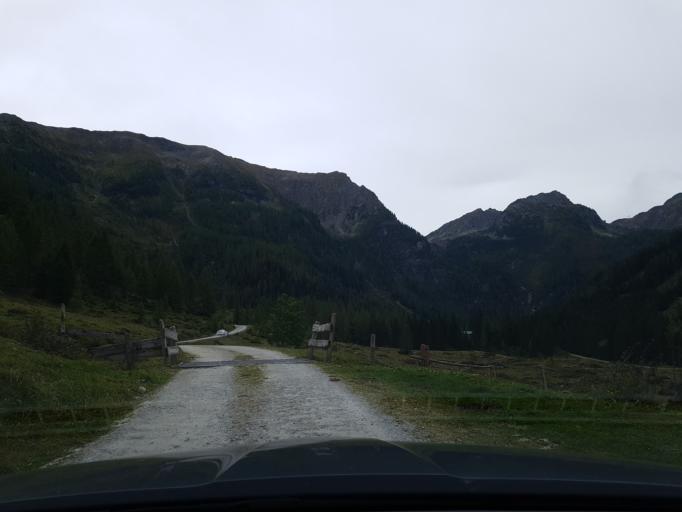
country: AT
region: Salzburg
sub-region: Politischer Bezirk Sankt Johann im Pongau
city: Untertauern
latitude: 47.2969
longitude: 13.5801
